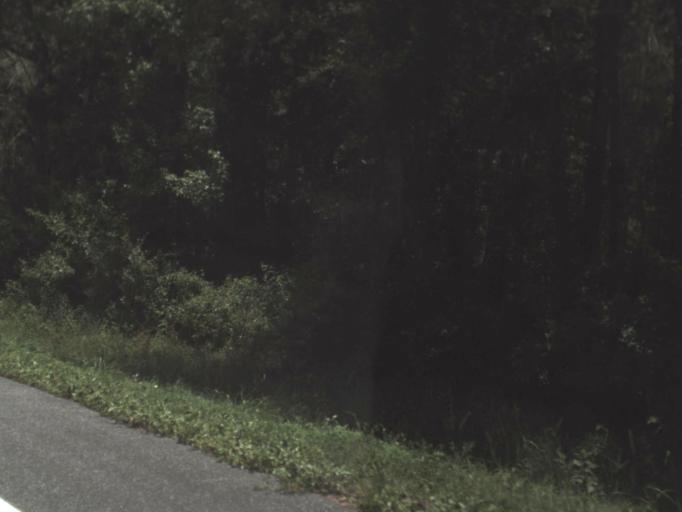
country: US
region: Florida
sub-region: Lafayette County
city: Mayo
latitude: 29.9797
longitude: -83.2018
